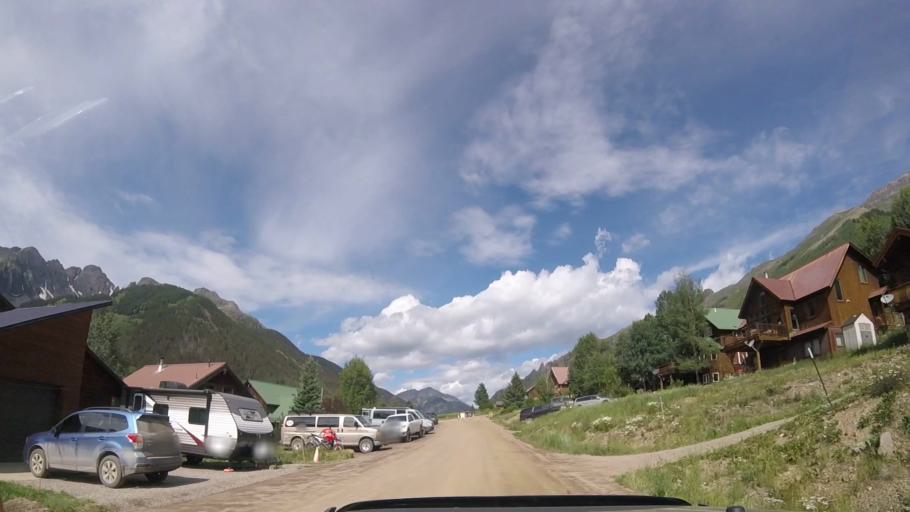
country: US
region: Colorado
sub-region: San Miguel County
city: Mountain Village
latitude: 37.8564
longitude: -107.8244
